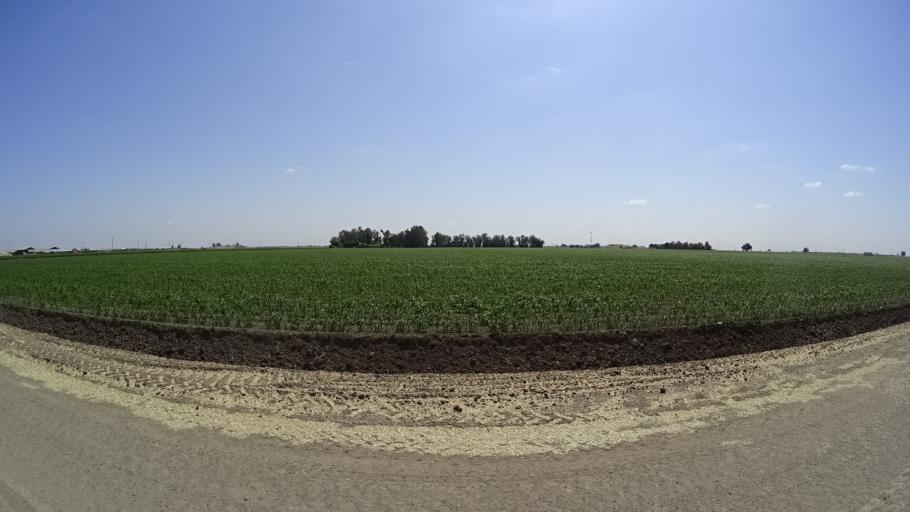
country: US
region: California
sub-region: Kings County
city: Home Garden
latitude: 36.2156
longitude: -119.6278
